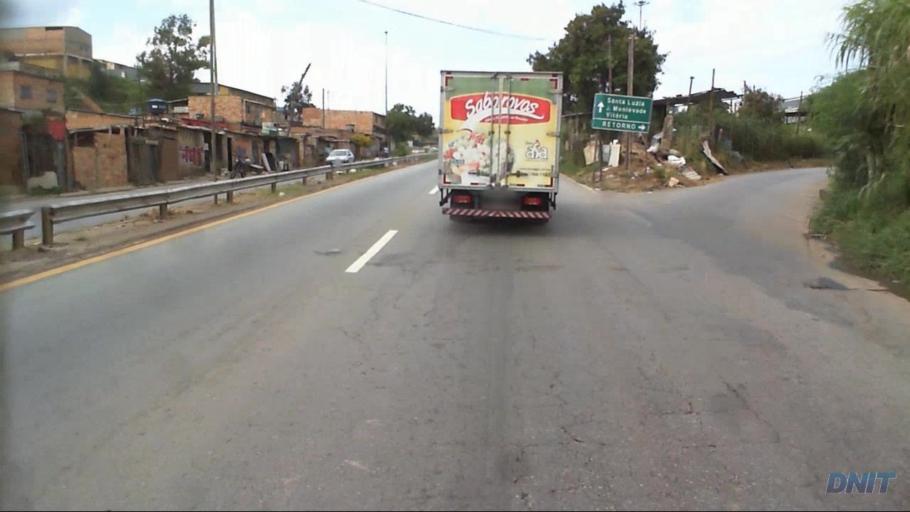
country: BR
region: Minas Gerais
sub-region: Belo Horizonte
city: Belo Horizonte
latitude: -19.8560
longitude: -43.8936
